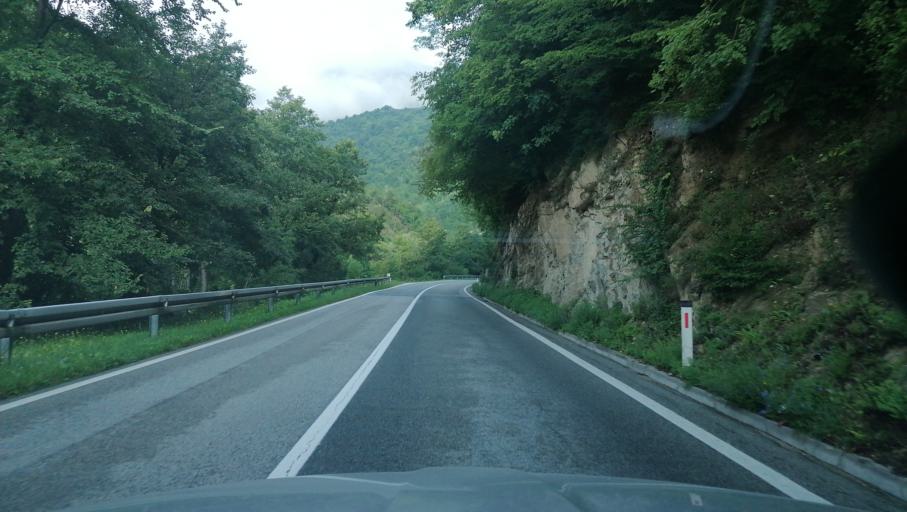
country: BA
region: Federation of Bosnia and Herzegovina
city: Jajce
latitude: 44.2869
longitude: 17.2577
